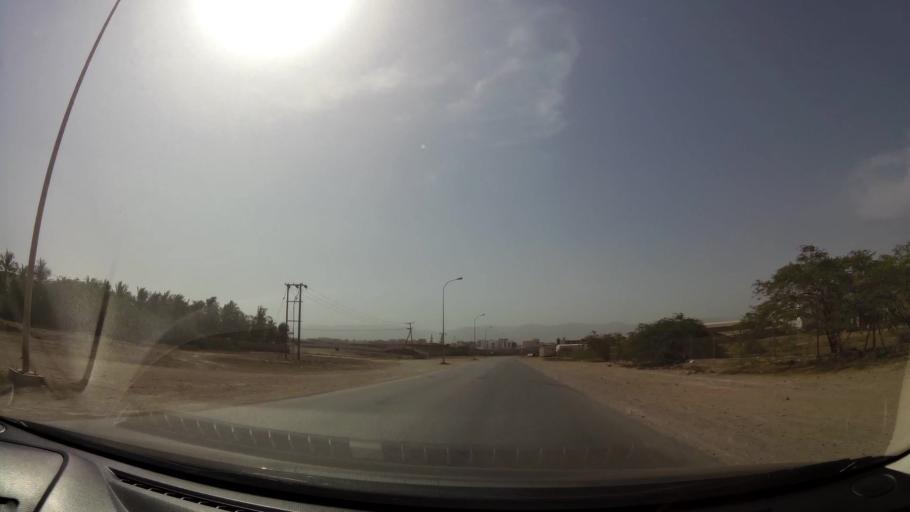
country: OM
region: Zufar
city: Salalah
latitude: 16.9936
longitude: 54.0206
